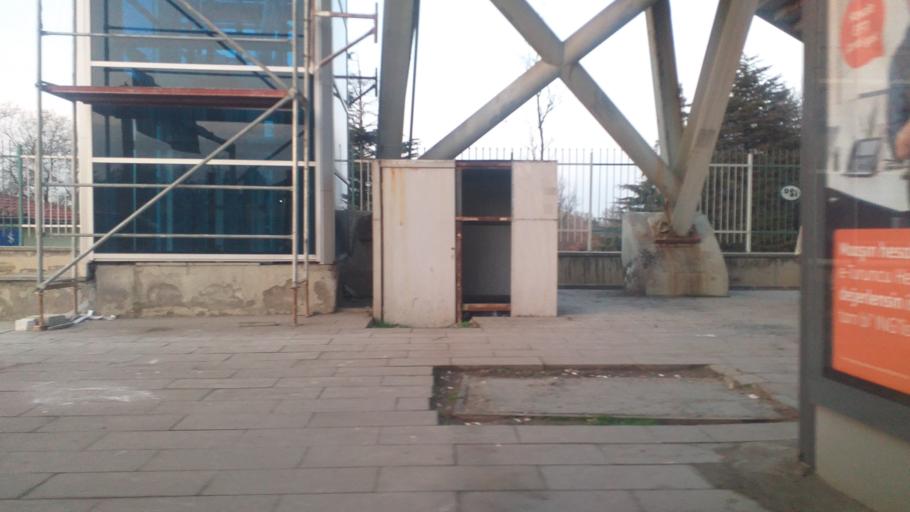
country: TR
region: Ankara
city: Ankara
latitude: 39.9613
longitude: 32.8456
